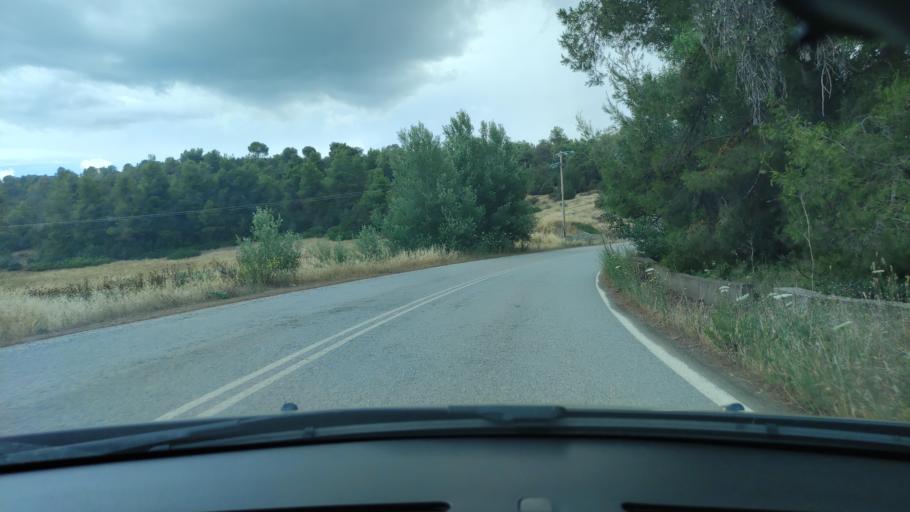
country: GR
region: Central Greece
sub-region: Nomos Evvoias
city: Afration
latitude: 38.5139
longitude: 23.7086
